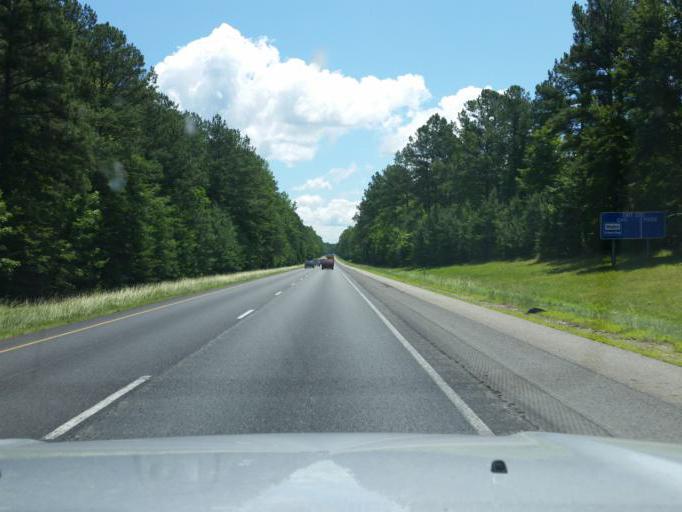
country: US
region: Virginia
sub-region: New Kent County
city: New Kent
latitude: 37.4849
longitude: -76.9505
